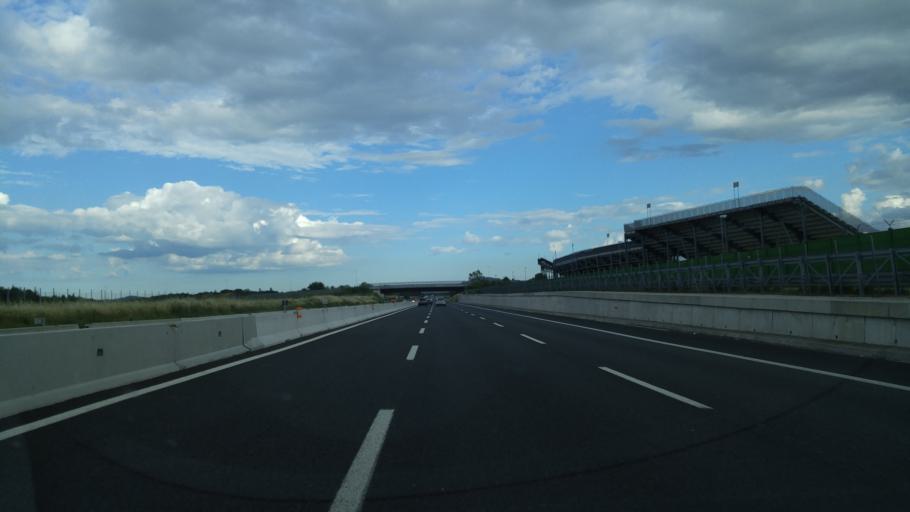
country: IT
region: Emilia-Romagna
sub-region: Provincia di Rimini
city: Santa Monica-Cella
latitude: 43.9657
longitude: 12.6886
